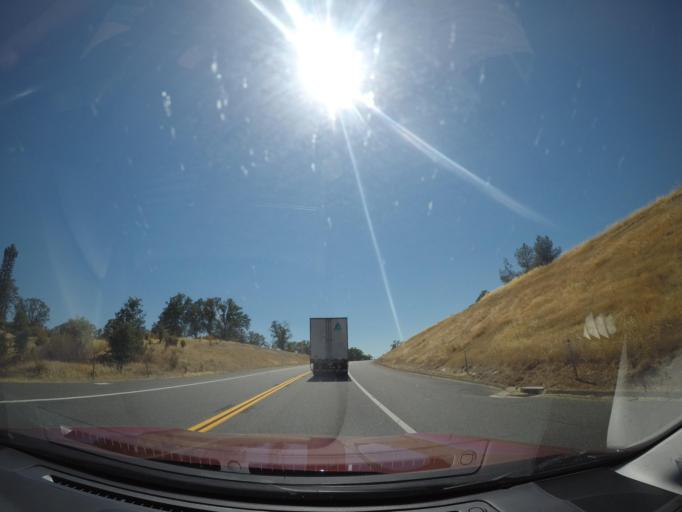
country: US
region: California
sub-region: Shasta County
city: Bella Vista
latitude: 40.6354
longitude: -122.2509
